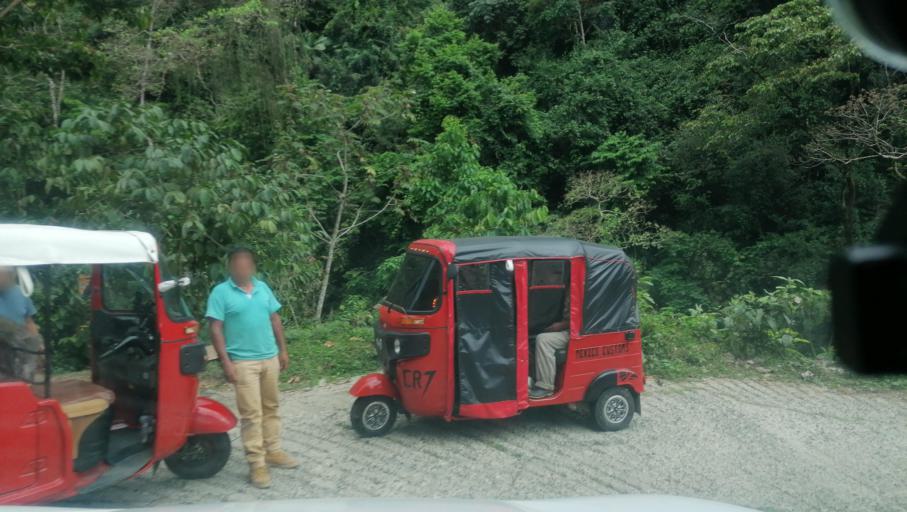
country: MX
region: Chiapas
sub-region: Cacahoatan
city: Benito Juarez
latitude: 15.1019
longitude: -92.1854
